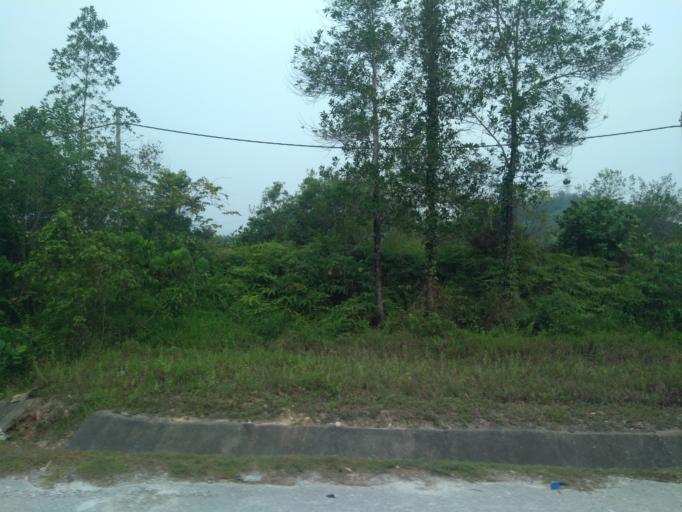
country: MY
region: Perak
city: Ipoh
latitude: 4.5524
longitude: 101.1652
